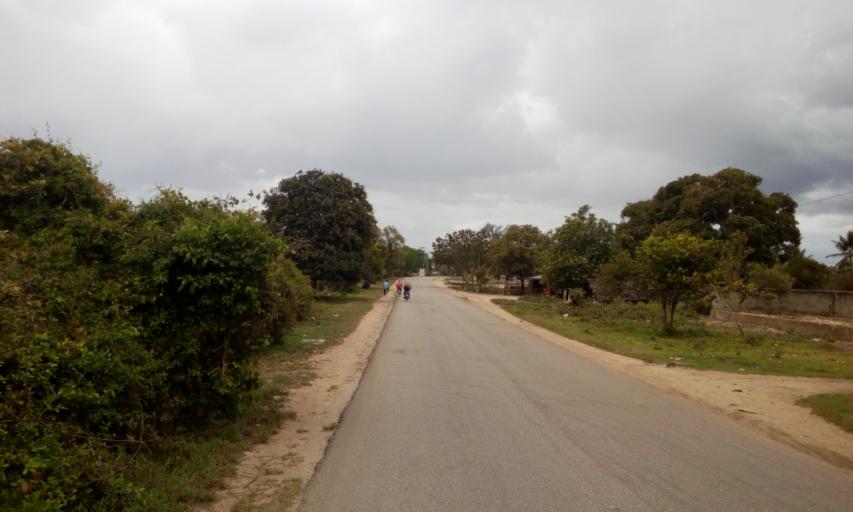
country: TZ
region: Zanzibar Central/South
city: Koani
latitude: -6.2001
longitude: 39.3114
